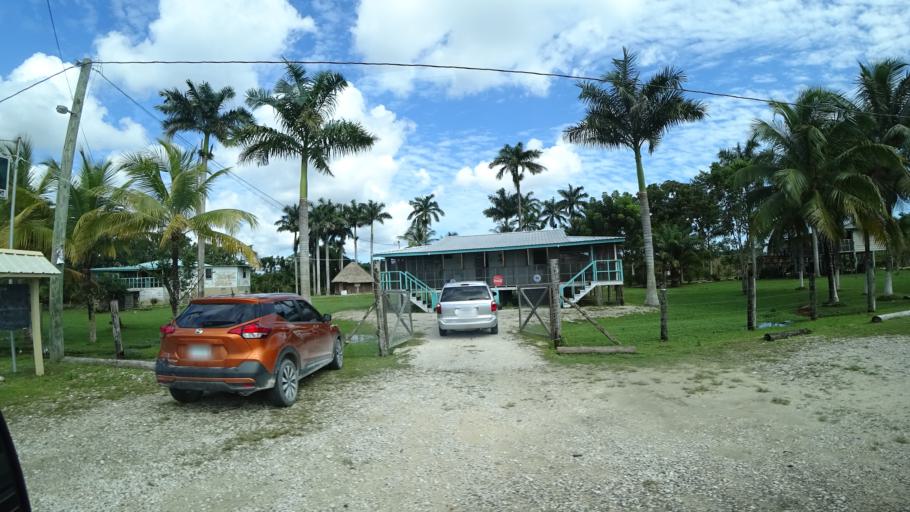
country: BZ
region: Belize
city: Belize City
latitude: 17.5702
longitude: -88.3876
